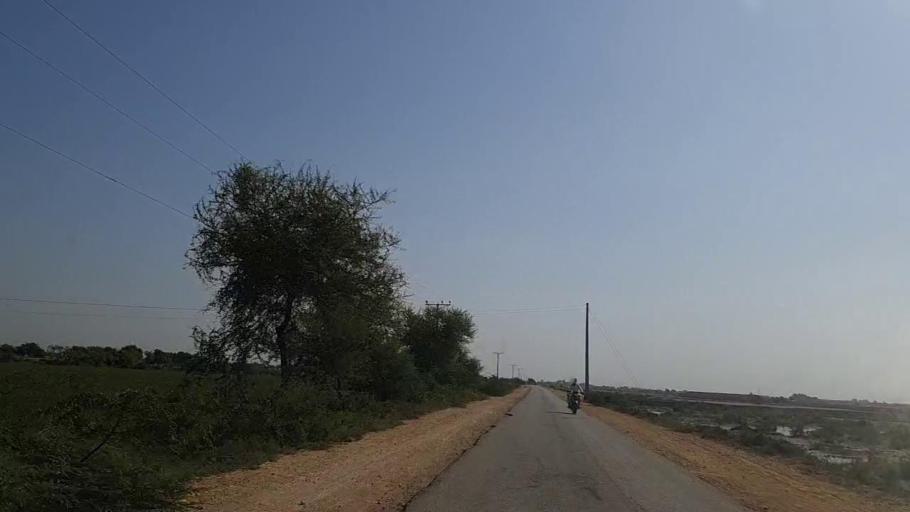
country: PK
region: Sindh
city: Mirpur Batoro
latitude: 24.6327
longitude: 68.2927
